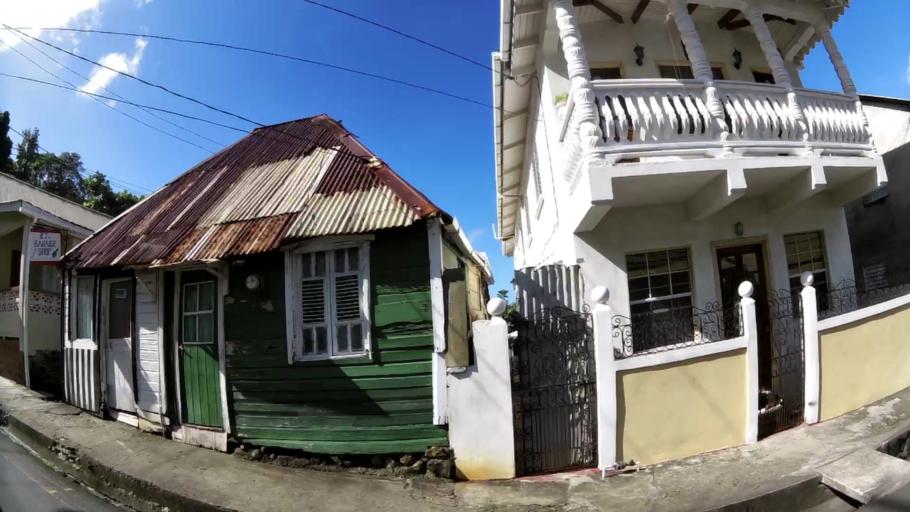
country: LC
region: Soufriere
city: Soufriere
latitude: 13.8529
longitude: -61.0578
